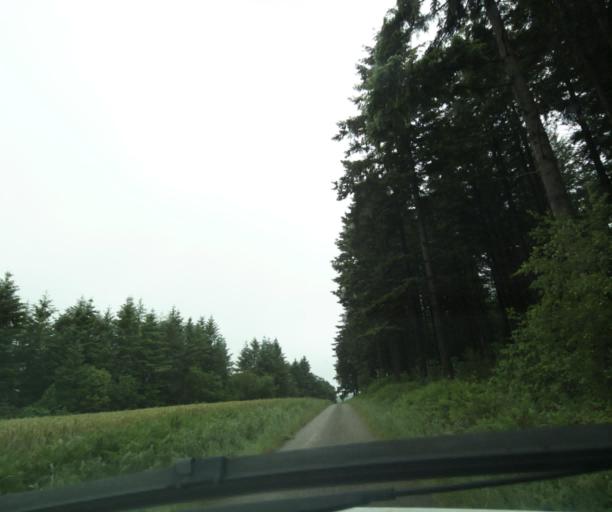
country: FR
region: Bourgogne
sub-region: Departement de Saone-et-Loire
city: Charolles
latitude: 46.4445
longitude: 4.3964
